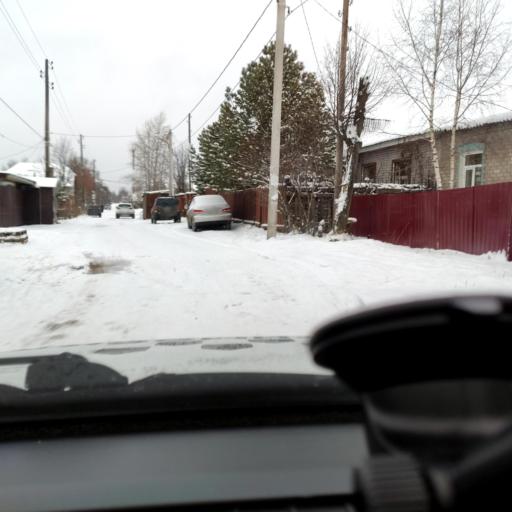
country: RU
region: Perm
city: Perm
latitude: 58.0563
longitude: 56.3612
